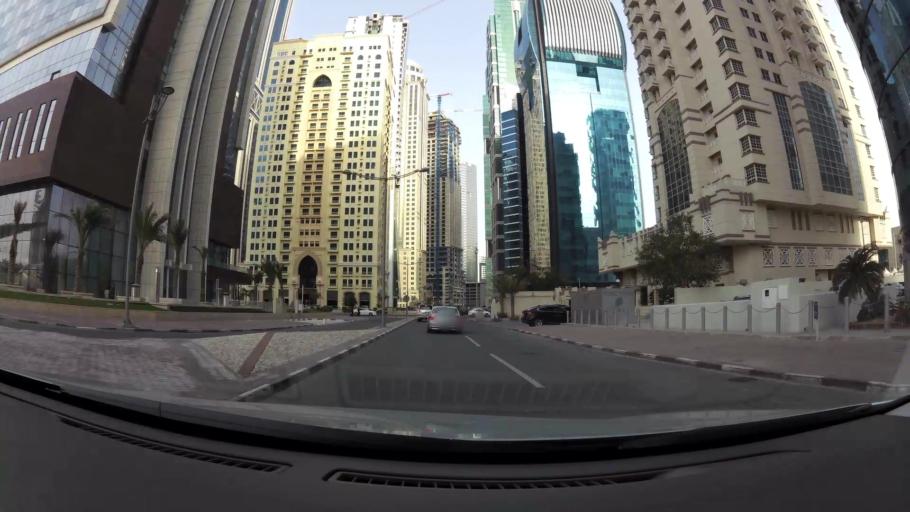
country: QA
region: Baladiyat ad Dawhah
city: Doha
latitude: 25.3274
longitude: 51.5287
